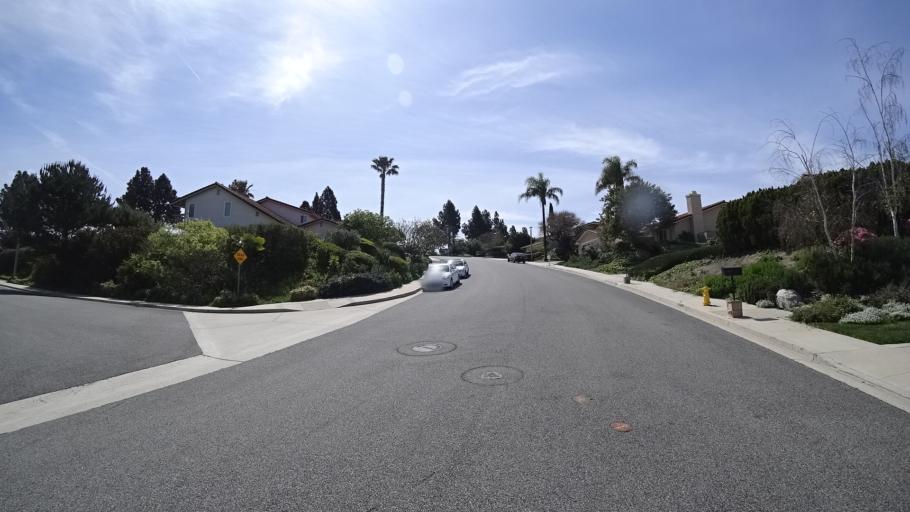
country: US
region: California
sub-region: Ventura County
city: Thousand Oaks
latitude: 34.2294
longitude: -118.8434
